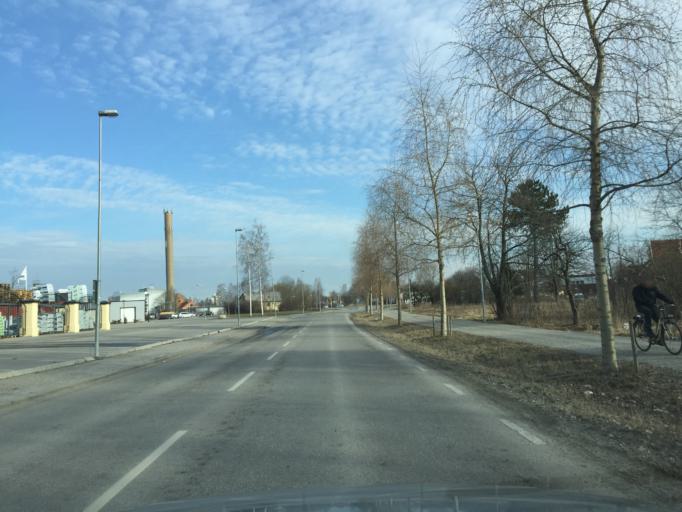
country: SE
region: OErebro
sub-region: Orebro Kommun
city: Orebro
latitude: 59.2631
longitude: 15.2395
